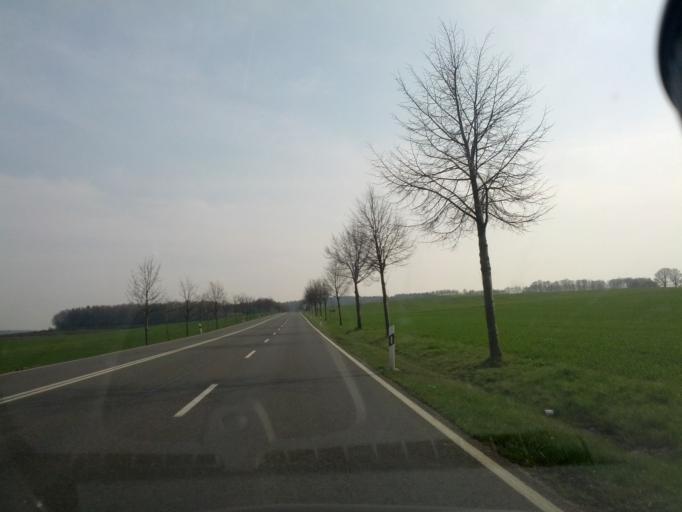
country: DE
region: Saxony
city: Kirchberg
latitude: 50.6435
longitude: 12.5658
